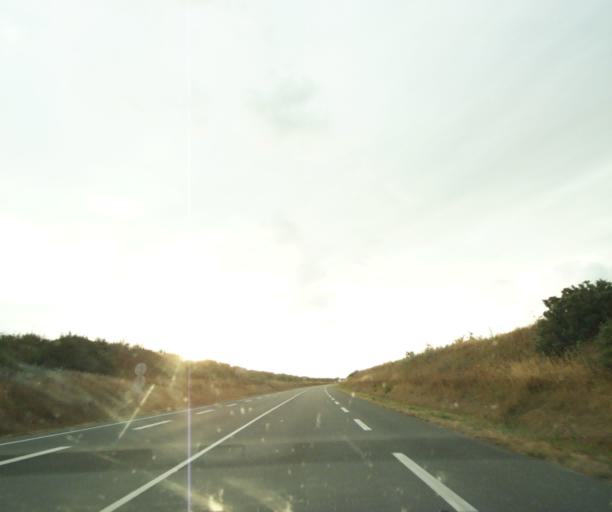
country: FR
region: Pays de la Loire
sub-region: Departement de la Vendee
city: Saint-Hilaire-de-Talmont
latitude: 46.4646
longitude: -1.6410
